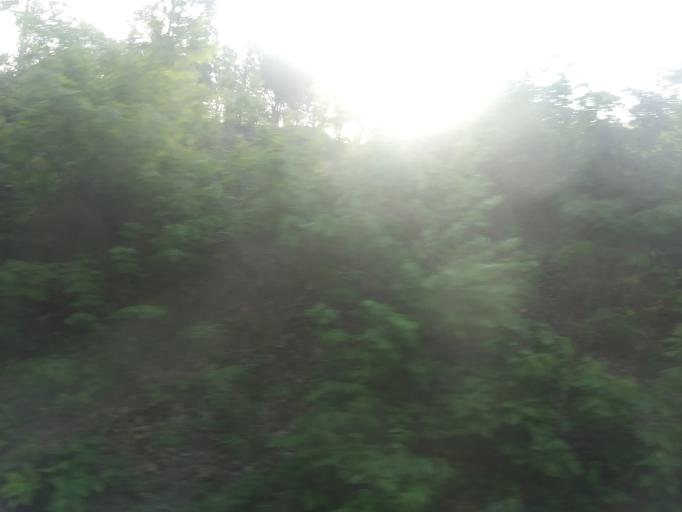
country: US
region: Massachusetts
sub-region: Franklin County
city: Buckland
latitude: 42.5831
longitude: -72.7734
